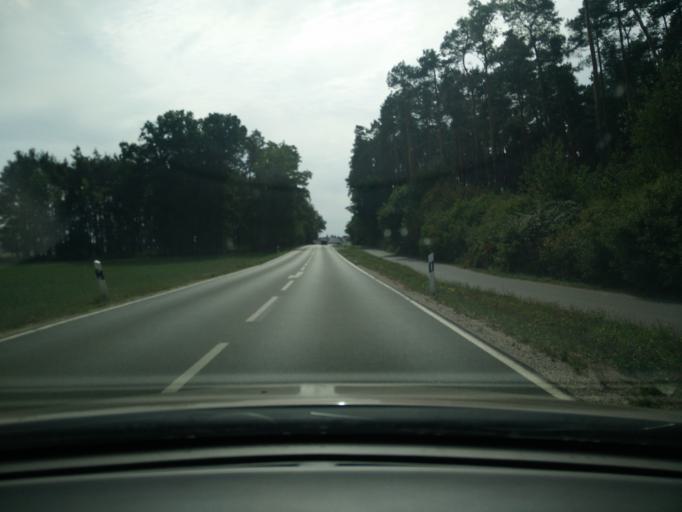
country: DE
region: Bavaria
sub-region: Regierungsbezirk Mittelfranken
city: Veitsbronn
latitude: 49.5001
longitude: 10.8795
